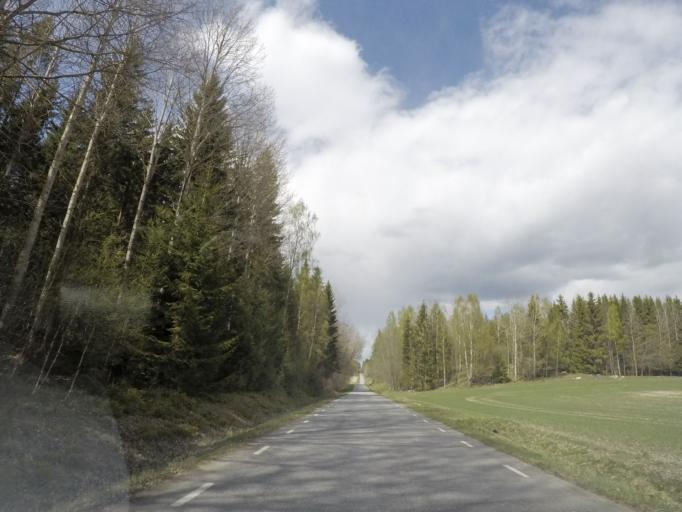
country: SE
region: Soedermanland
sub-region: Katrineholms Kommun
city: Katrineholm
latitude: 58.9272
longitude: 16.3211
